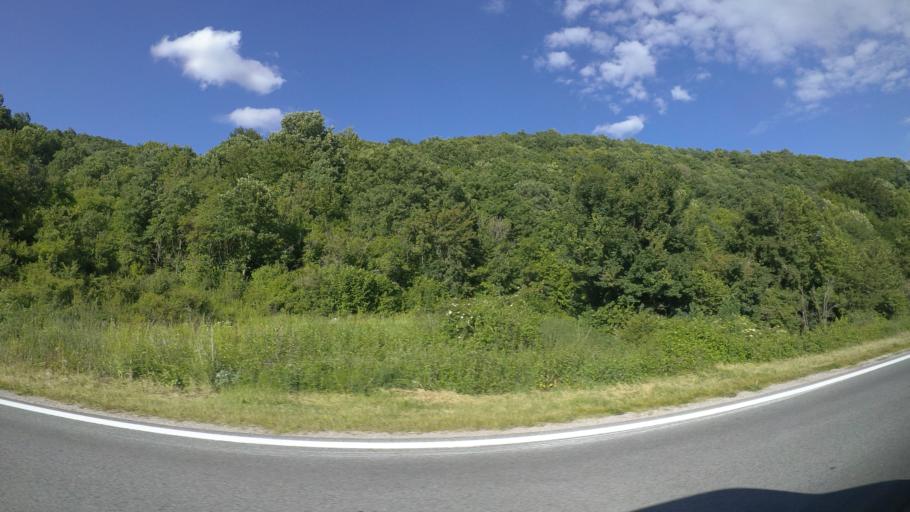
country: BA
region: Federation of Bosnia and Herzegovina
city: Bihac
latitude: 44.6247
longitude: 15.7361
